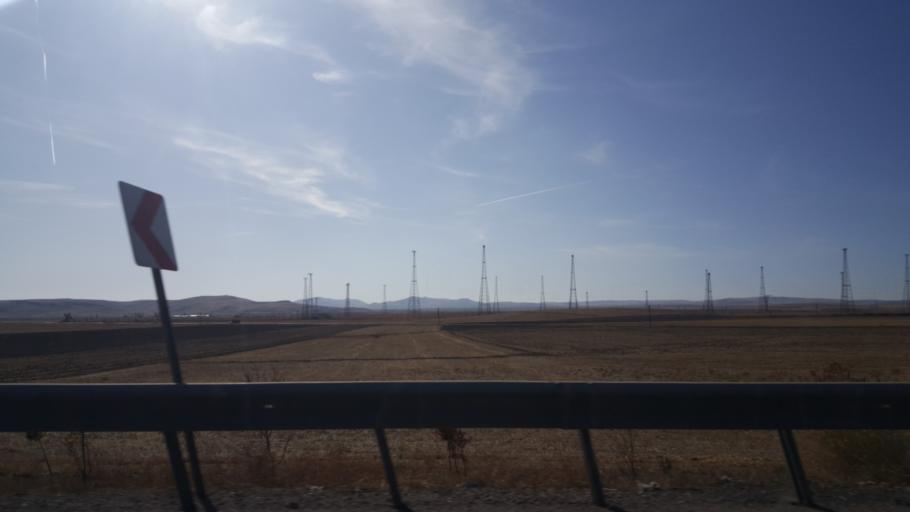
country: TR
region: Ankara
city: Yenice
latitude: 39.4059
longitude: 32.8719
